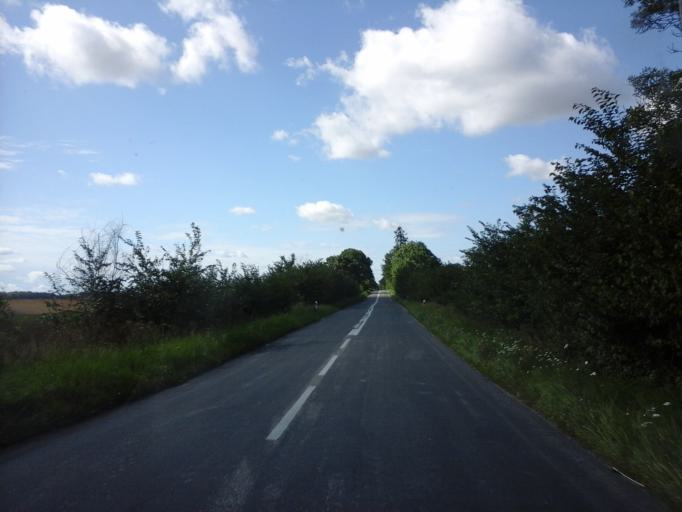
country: PL
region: West Pomeranian Voivodeship
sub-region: Powiat stargardzki
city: Suchan
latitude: 53.2152
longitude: 15.2893
